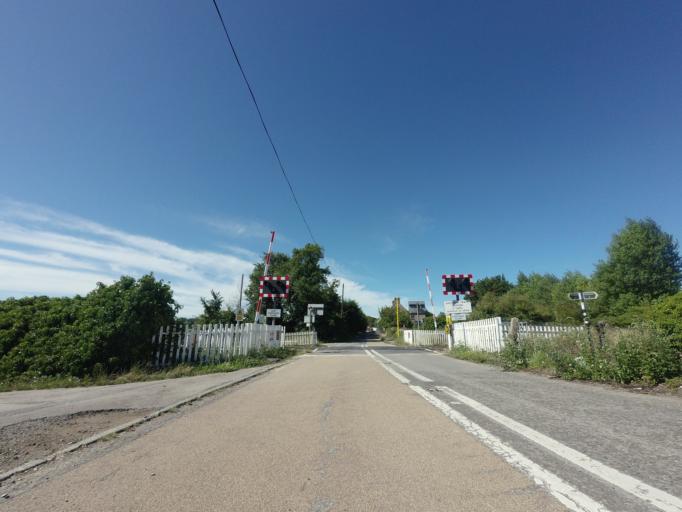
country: GB
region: England
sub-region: Kent
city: Sandwich
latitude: 51.3274
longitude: 1.3473
